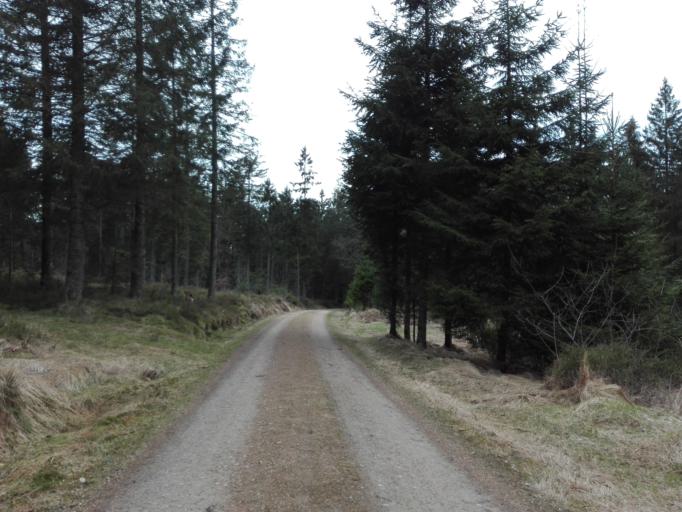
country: AT
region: Upper Austria
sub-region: Politischer Bezirk Rohrbach
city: Ulrichsberg
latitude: 48.7018
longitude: 13.9516
